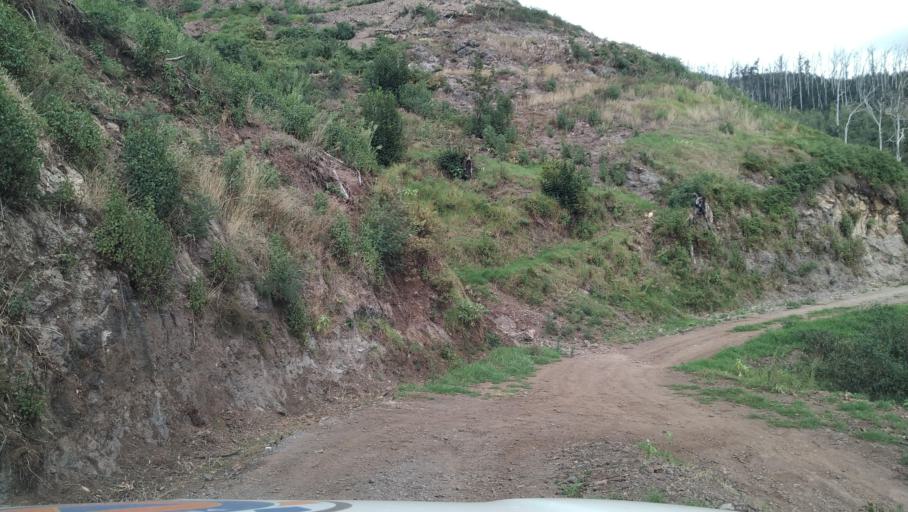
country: PT
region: Madeira
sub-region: Funchal
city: Nossa Senhora do Monte
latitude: 32.6795
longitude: -16.9283
